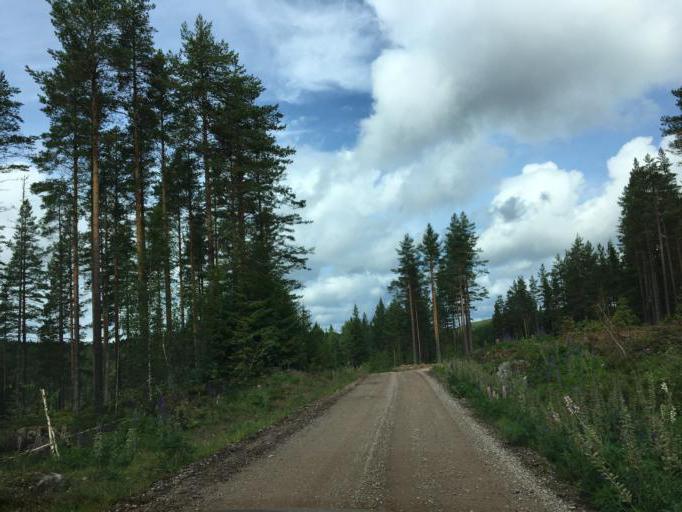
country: SE
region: OErebro
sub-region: Hallefors Kommun
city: Haellefors
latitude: 60.0694
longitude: 14.4768
